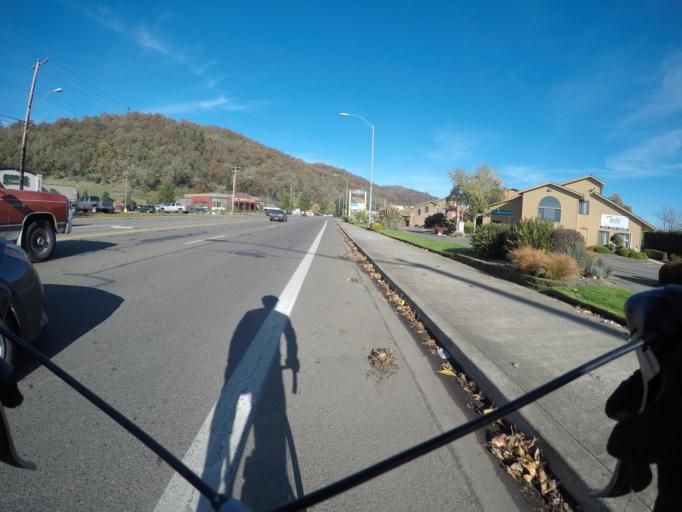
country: US
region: Oregon
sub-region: Douglas County
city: Roseburg
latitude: 43.2348
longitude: -123.3723
